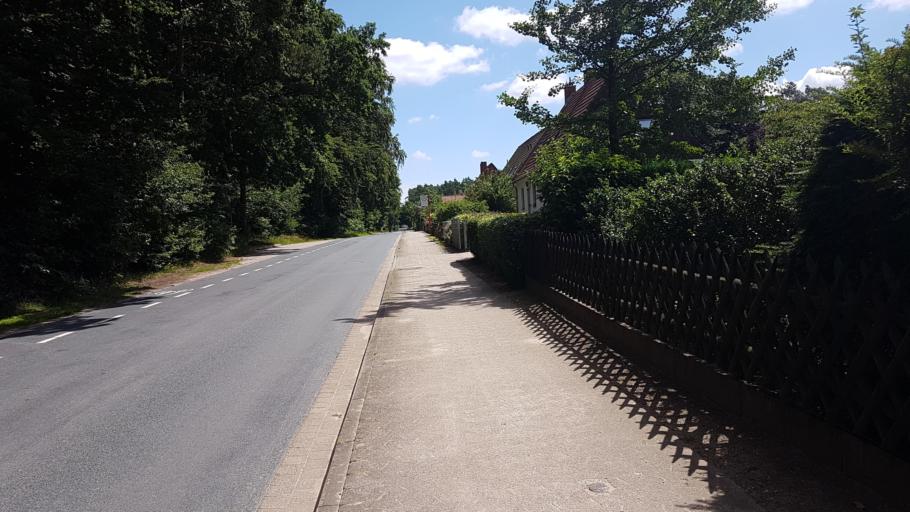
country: DE
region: Lower Saxony
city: Rullstorf
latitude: 53.2836
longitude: 10.5359
